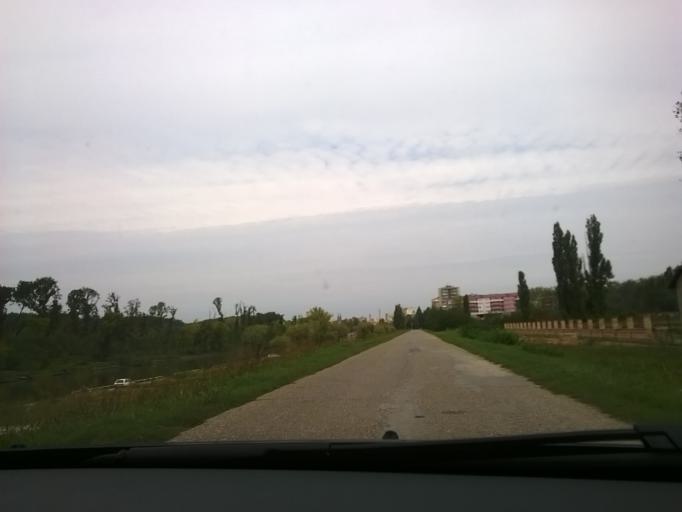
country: RS
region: Autonomna Pokrajina Vojvodina
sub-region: Juznobanatski Okrug
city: Pancevo
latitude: 44.8590
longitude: 20.6387
